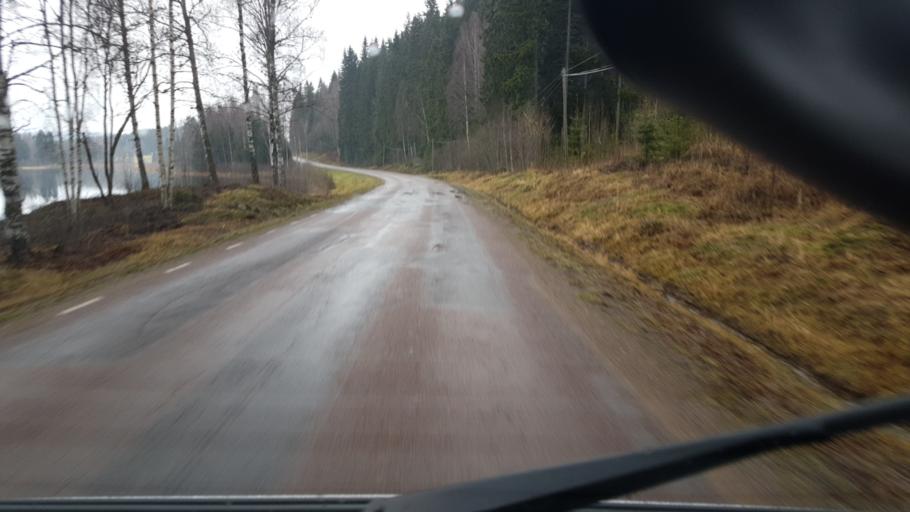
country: SE
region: Vaermland
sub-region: Eda Kommun
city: Amotfors
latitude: 59.8989
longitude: 12.5255
